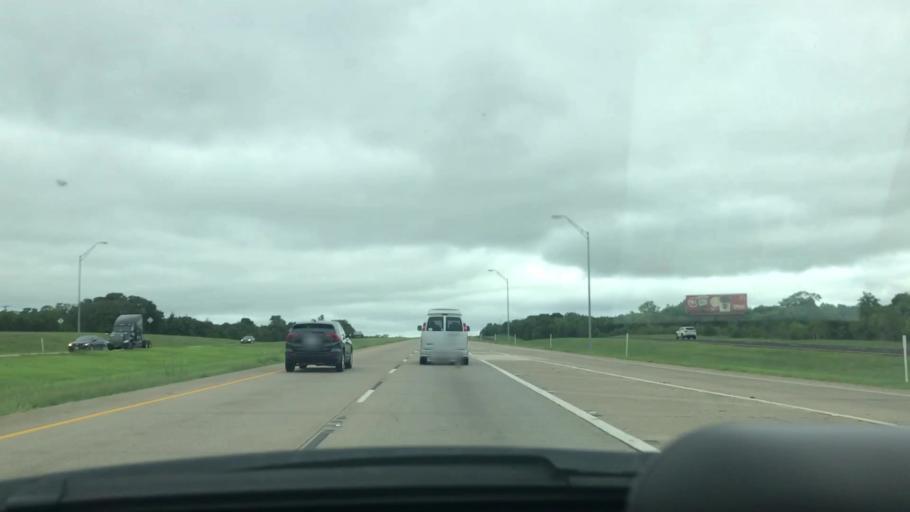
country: US
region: Texas
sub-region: Grayson County
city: Denison
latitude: 33.7331
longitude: -96.5852
